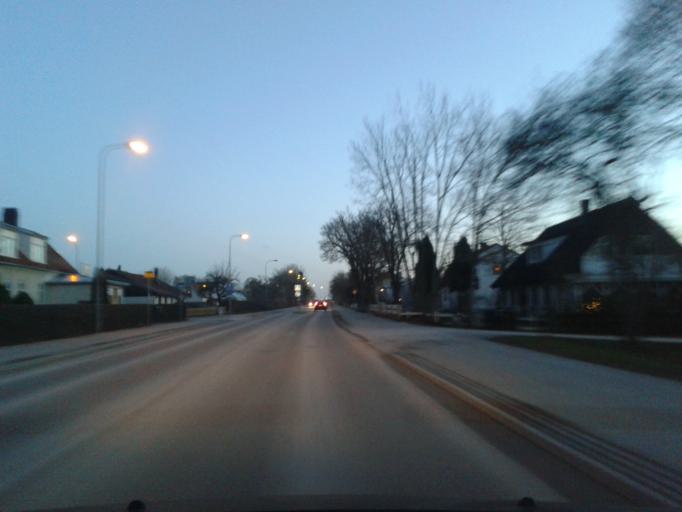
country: SE
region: Gotland
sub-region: Gotland
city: Visby
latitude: 57.6308
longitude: 18.3138
